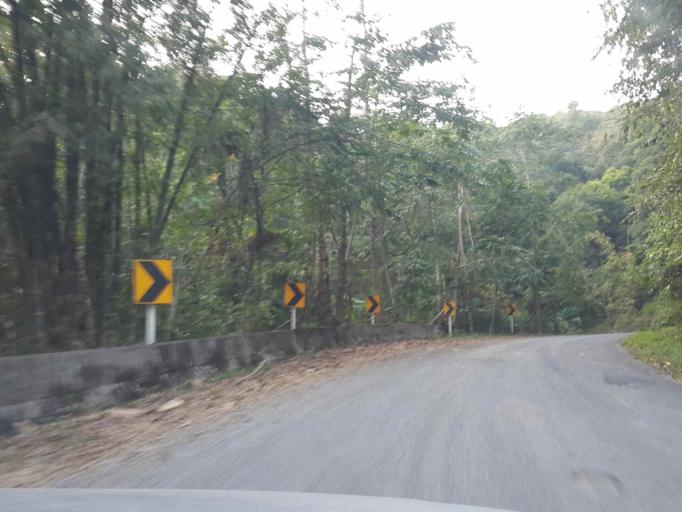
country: TH
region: Chiang Mai
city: Mae On
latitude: 18.9929
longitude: 99.3428
